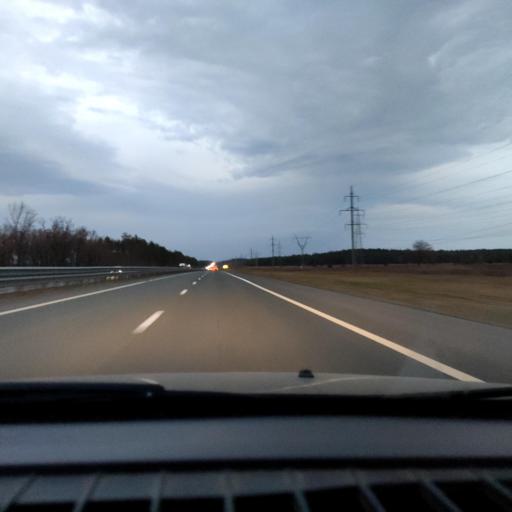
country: RU
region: Samara
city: Povolzhskiy
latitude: 53.5148
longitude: 49.6544
